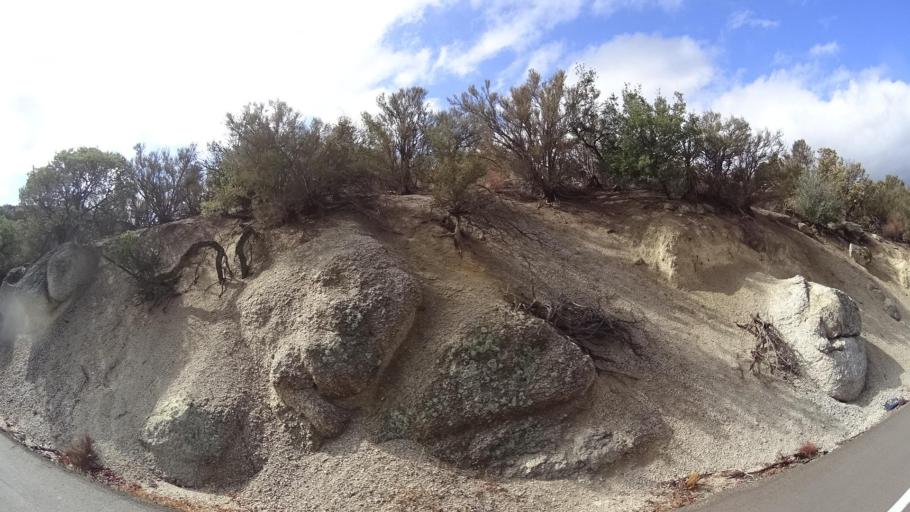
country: US
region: California
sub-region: San Diego County
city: Campo
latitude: 32.7226
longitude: -116.4120
